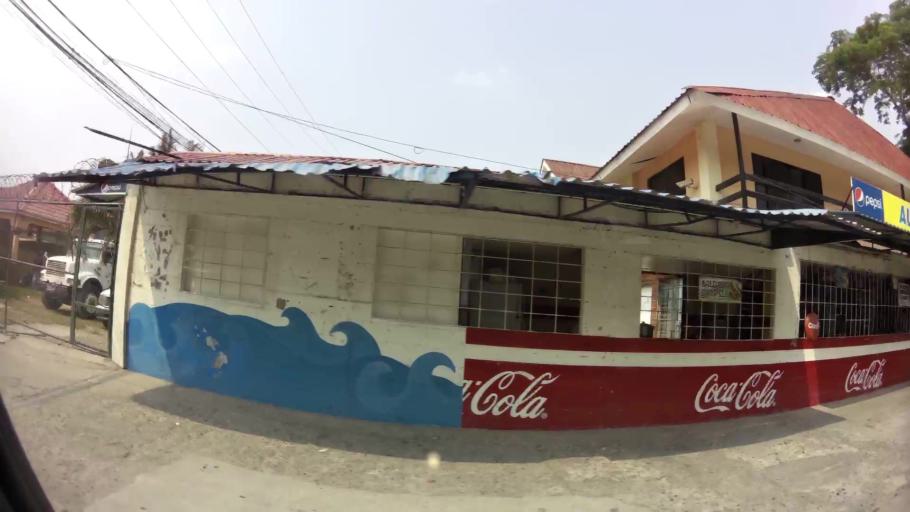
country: HN
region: Cortes
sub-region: San Pedro Sula
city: Pena Blanca
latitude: 15.5502
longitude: -88.0273
